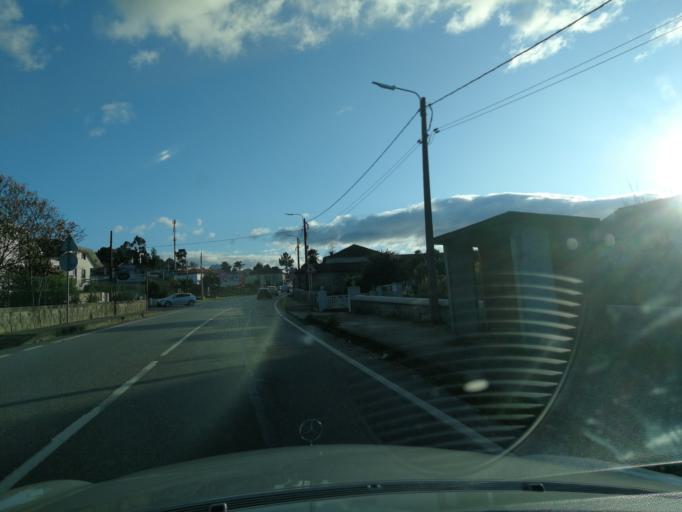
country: PT
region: Braga
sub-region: Esposende
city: Marinhas
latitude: 41.6081
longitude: -8.7404
